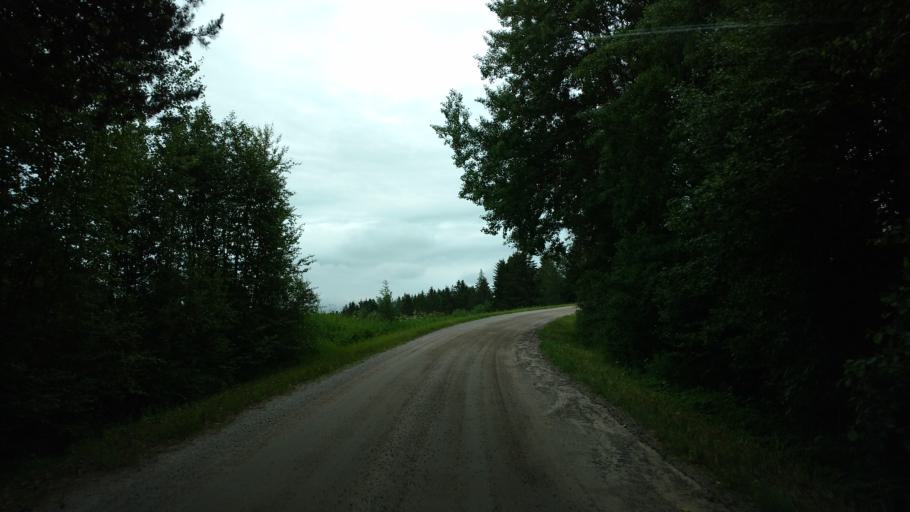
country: FI
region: Varsinais-Suomi
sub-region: Salo
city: Halikko
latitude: 60.4765
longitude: 23.0026
